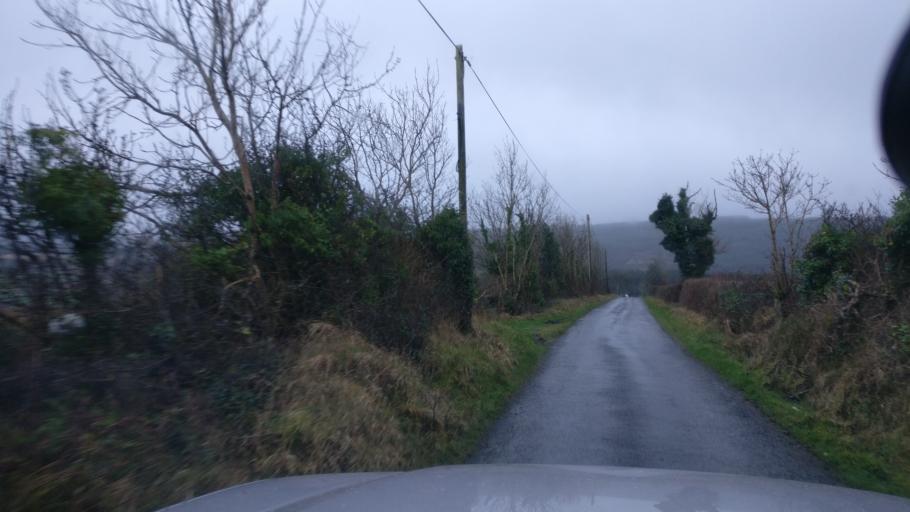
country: IE
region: Connaught
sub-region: County Galway
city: Loughrea
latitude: 53.1555
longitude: -8.6373
